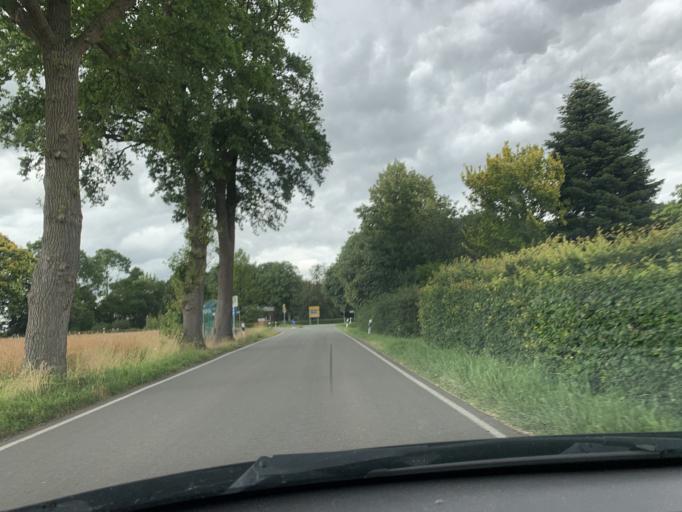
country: DE
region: Lower Saxony
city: Westerstede
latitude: 53.2250
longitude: 7.9017
